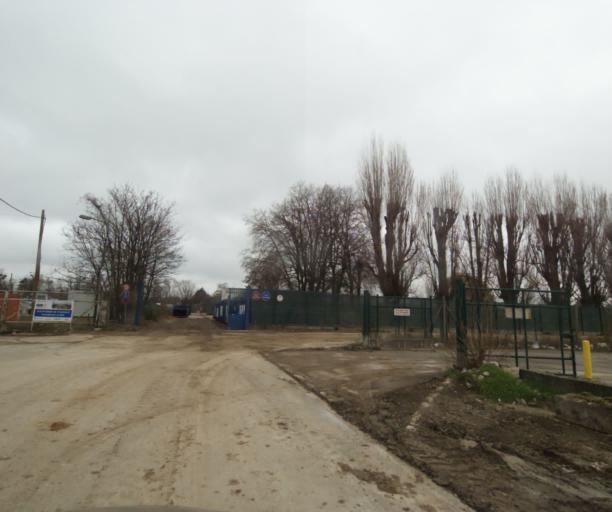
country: FR
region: Ile-de-France
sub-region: Departement du Val-de-Marne
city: Ablon-sur-Seine
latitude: 48.7386
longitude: 2.4329
